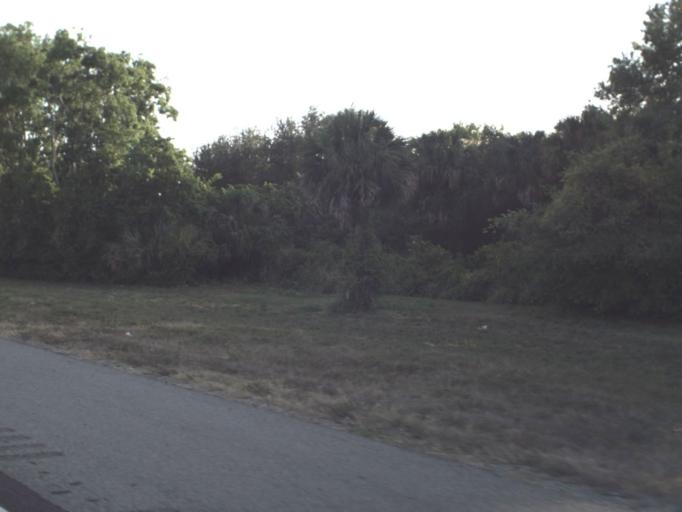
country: US
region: Florida
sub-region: Brevard County
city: Port Saint John
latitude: 28.4722
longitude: -80.8213
